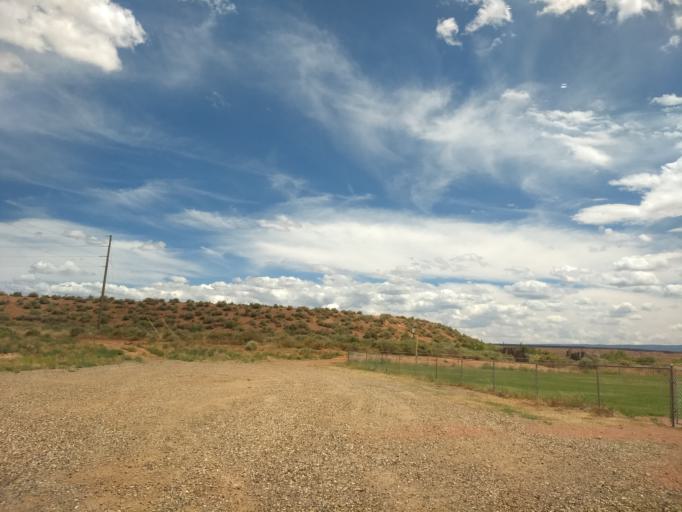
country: US
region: Arizona
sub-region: Coconino County
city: Fredonia
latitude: 36.9568
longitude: -112.5231
